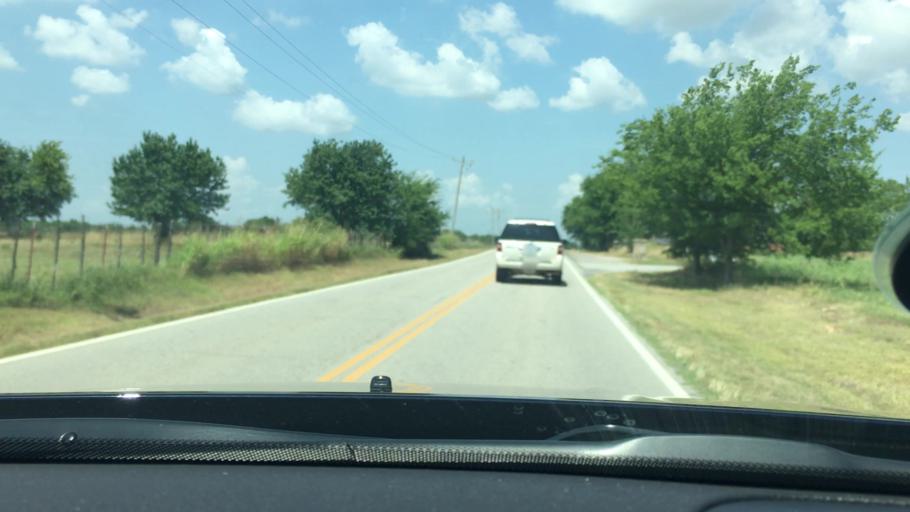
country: US
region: Oklahoma
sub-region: Bryan County
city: Durant
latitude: 34.0848
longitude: -96.4202
